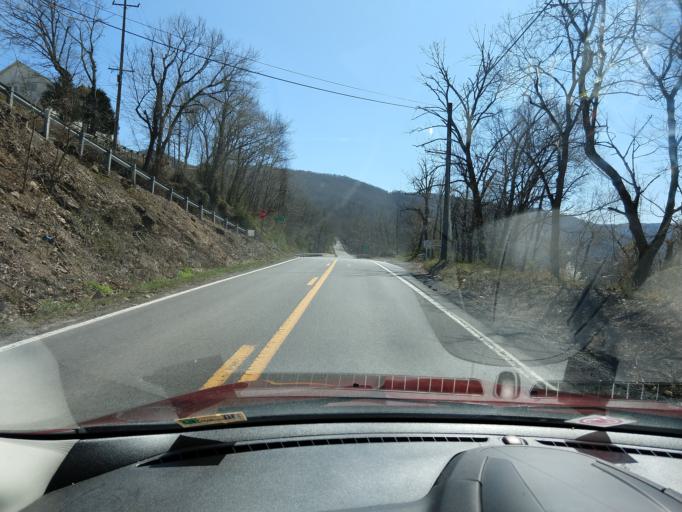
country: US
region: West Virginia
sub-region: Summers County
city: Hinton
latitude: 37.7710
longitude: -80.8915
